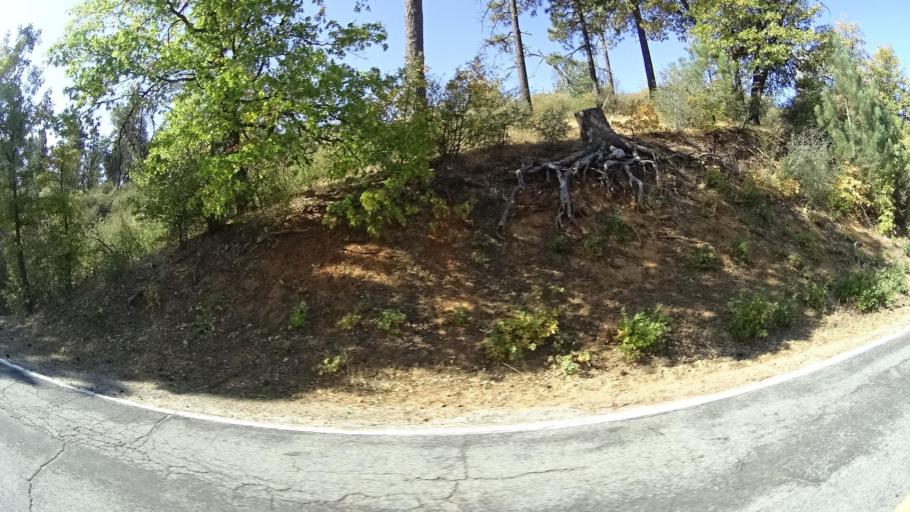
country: US
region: California
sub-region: San Diego County
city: Pine Valley
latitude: 32.8905
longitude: -116.4437
